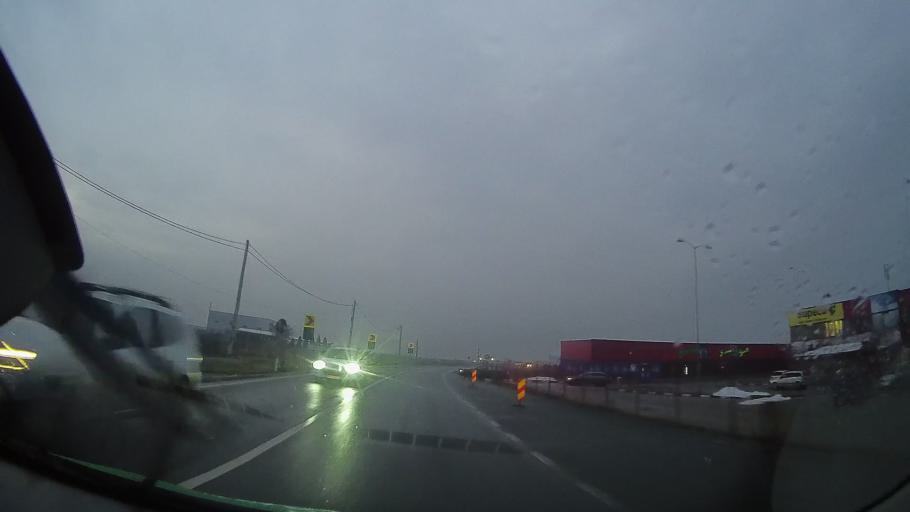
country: RO
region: Harghita
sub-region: Municipiul Gheorgheni
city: Gheorgheni
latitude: 46.7284
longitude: 25.5808
